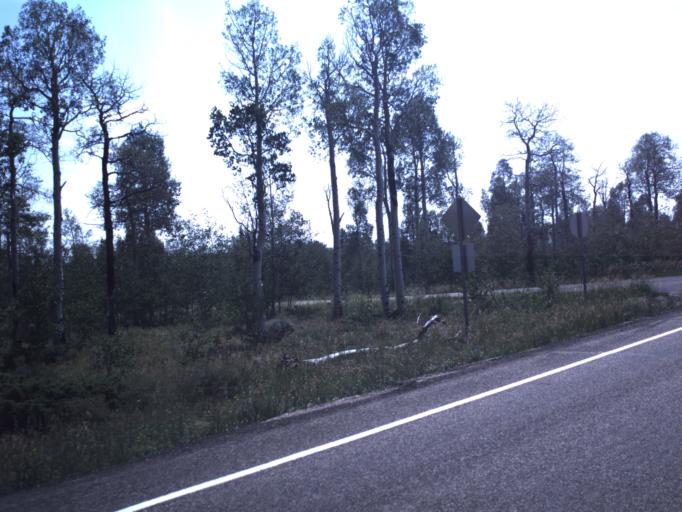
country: US
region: Utah
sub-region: Uintah County
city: Maeser
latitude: 40.7266
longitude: -109.4694
